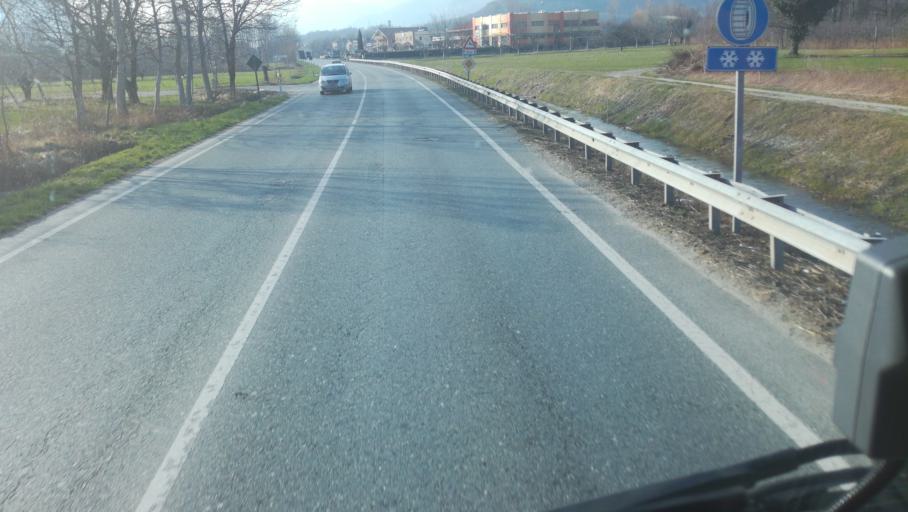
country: IT
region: Piedmont
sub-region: Provincia di Torino
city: Villar Dora
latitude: 45.1001
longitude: 7.3961
